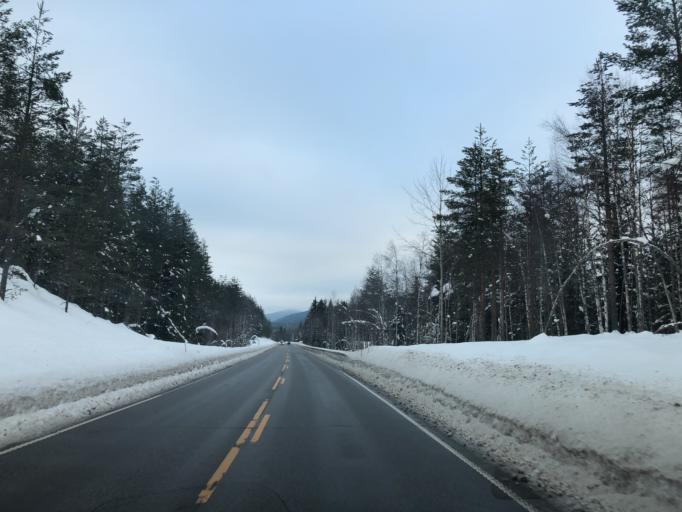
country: NO
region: Hedmark
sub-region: Trysil
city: Innbygda
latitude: 61.2641
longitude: 12.3081
